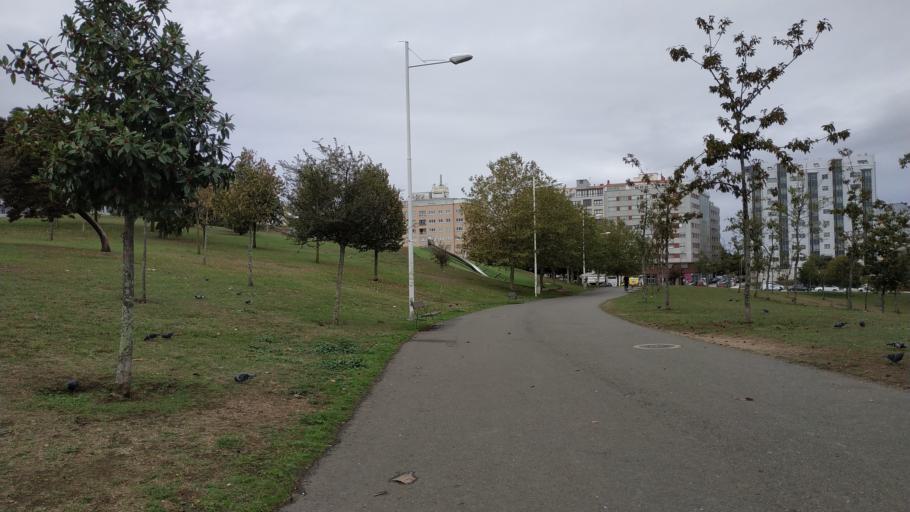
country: ES
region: Galicia
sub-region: Provincia da Coruna
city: A Coruna
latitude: 43.3459
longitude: -8.3951
